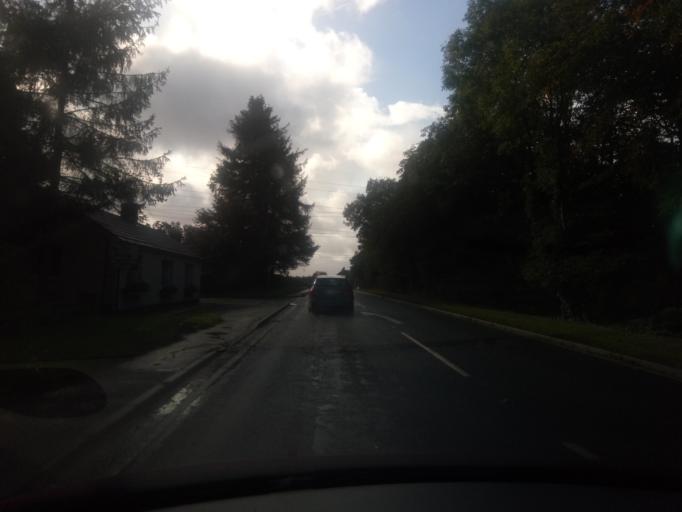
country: GB
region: England
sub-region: Cumbria
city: Carlisle
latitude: 54.9426
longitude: -2.9438
